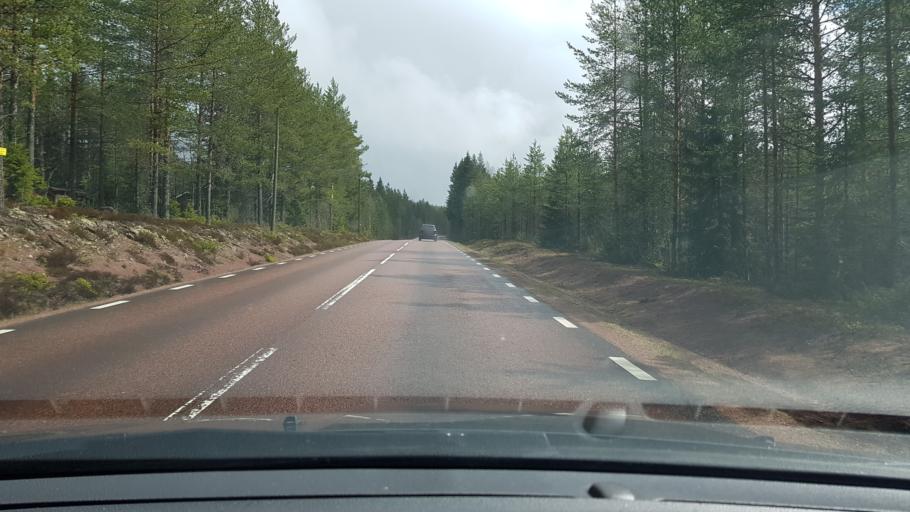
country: SE
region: Dalarna
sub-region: Malung-Saelens kommun
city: Malung
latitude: 61.0598
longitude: 13.3489
